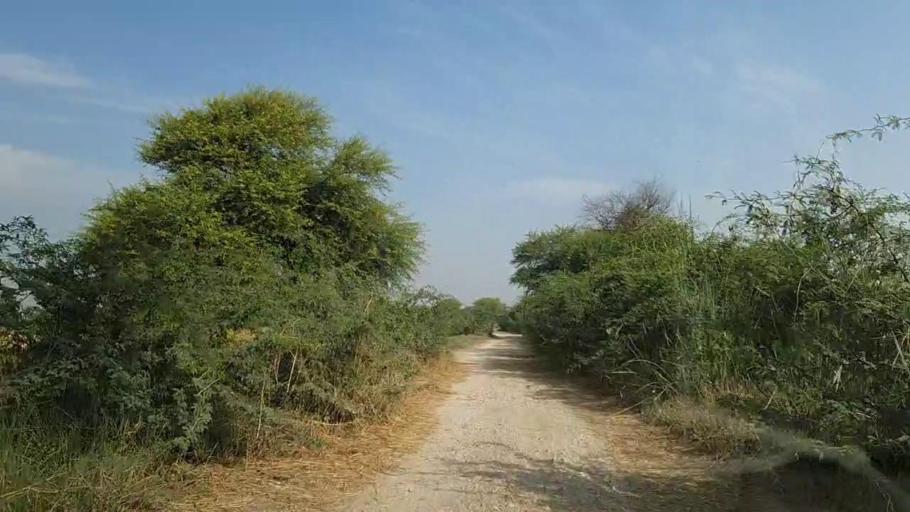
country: PK
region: Sindh
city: Mirpur Batoro
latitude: 24.7105
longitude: 68.2231
